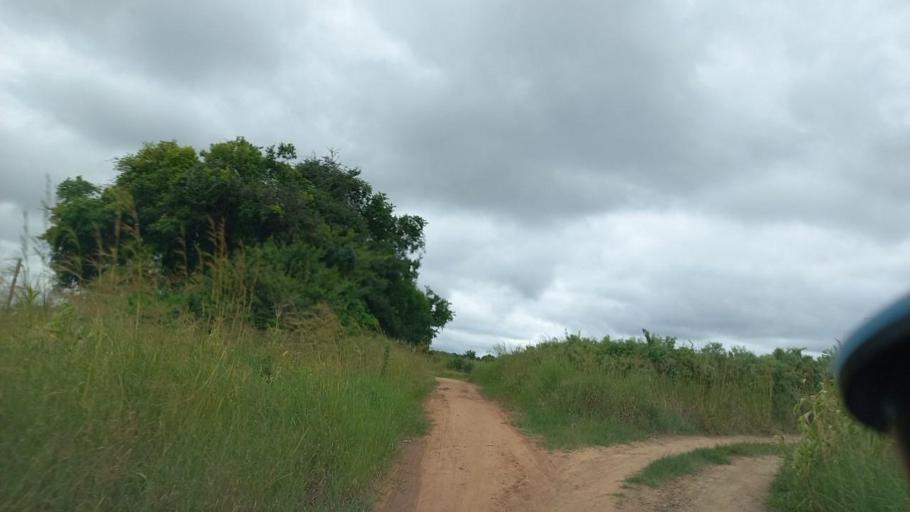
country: ZM
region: Lusaka
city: Lusaka
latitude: -15.1213
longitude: 28.3719
